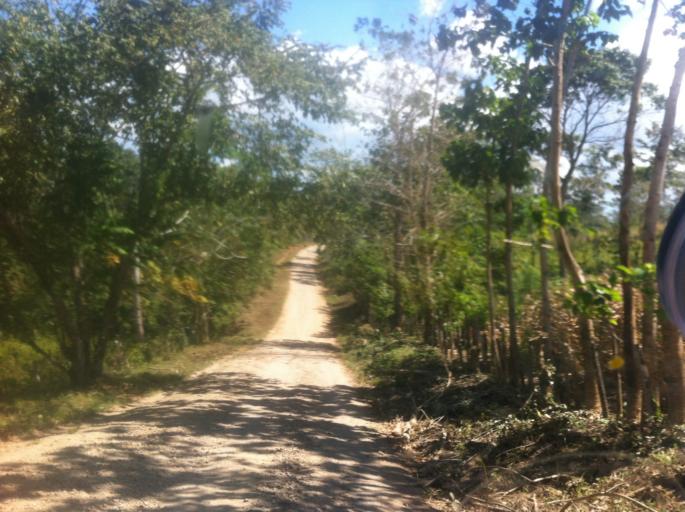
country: NI
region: Rio San Juan
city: San Carlos
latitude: 11.2380
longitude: -84.5214
